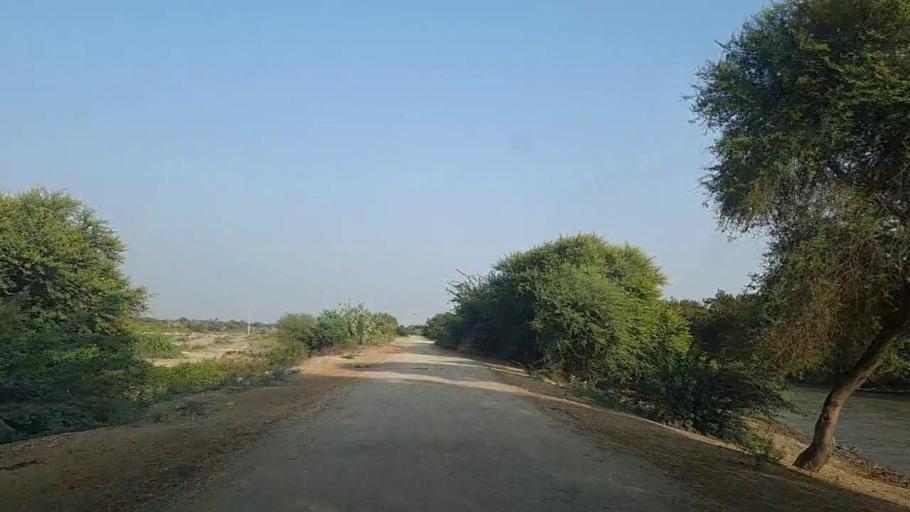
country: PK
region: Sindh
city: Mirpur Sakro
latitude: 24.5745
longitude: 67.6813
